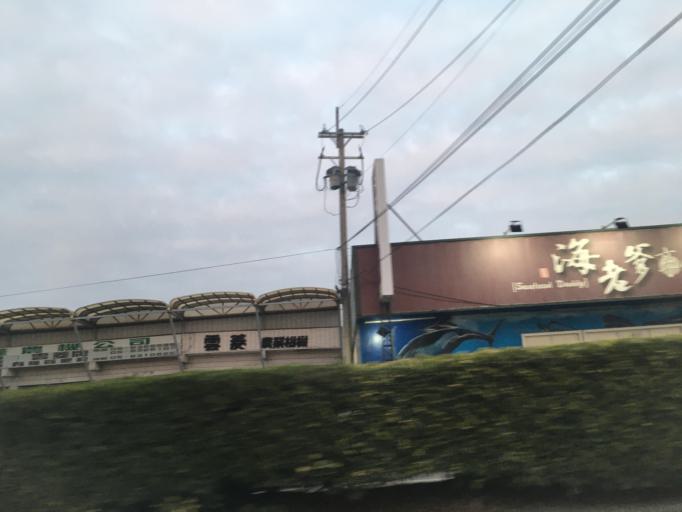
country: TW
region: Taiwan
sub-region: Yunlin
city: Douliu
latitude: 23.7016
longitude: 120.4584
